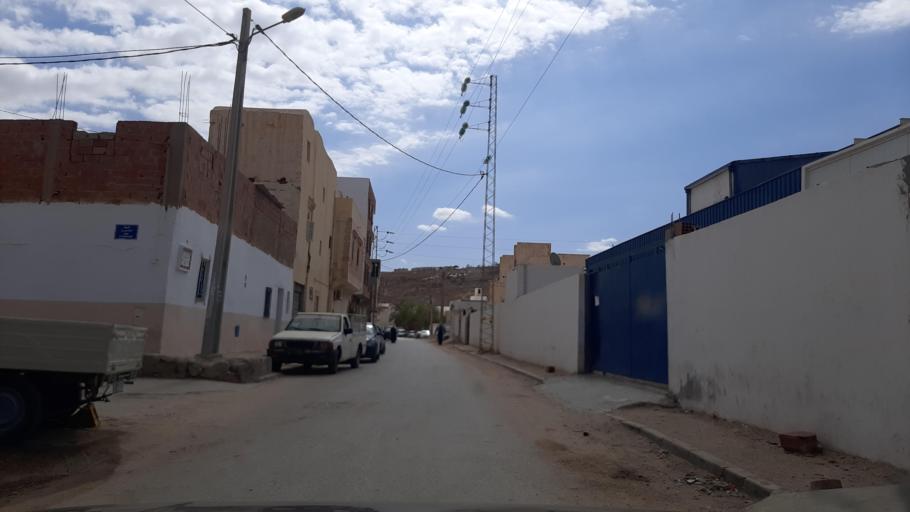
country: TN
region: Tataouine
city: Tataouine
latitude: 32.9309
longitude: 10.4446
